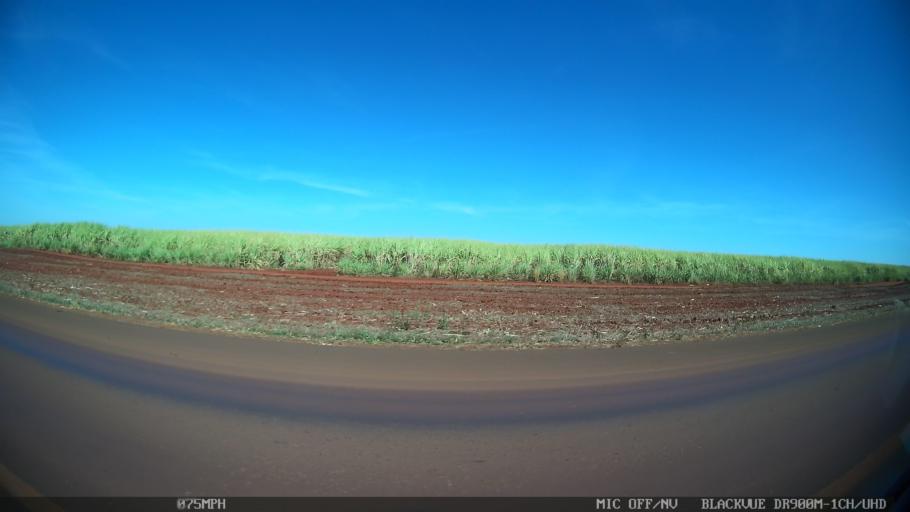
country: BR
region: Sao Paulo
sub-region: Ipua
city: Ipua
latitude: -20.4975
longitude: -47.9659
